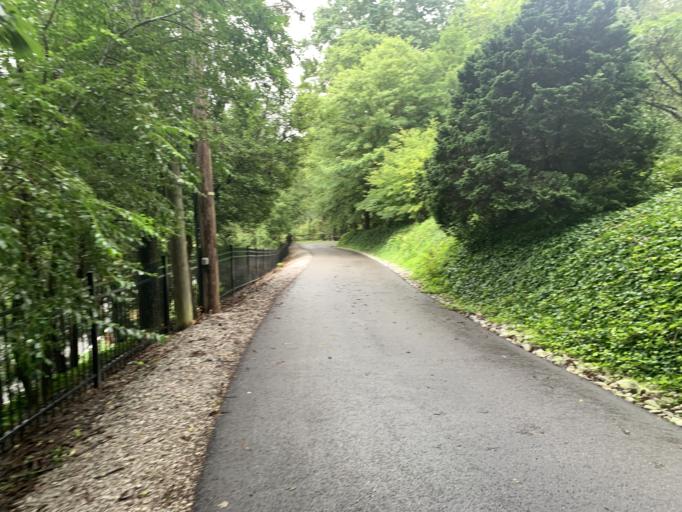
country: US
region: West Virginia
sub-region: Kanawha County
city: Charleston
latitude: 38.3423
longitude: -81.6384
